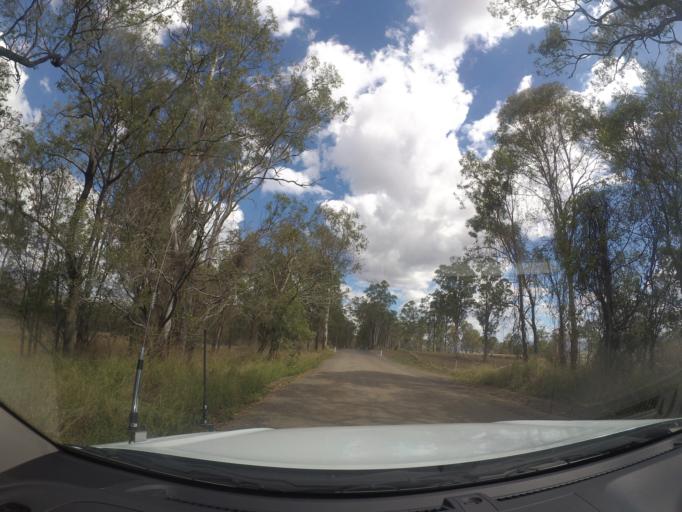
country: AU
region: Queensland
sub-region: Logan
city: Cedar Vale
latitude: -27.9017
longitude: 152.9866
